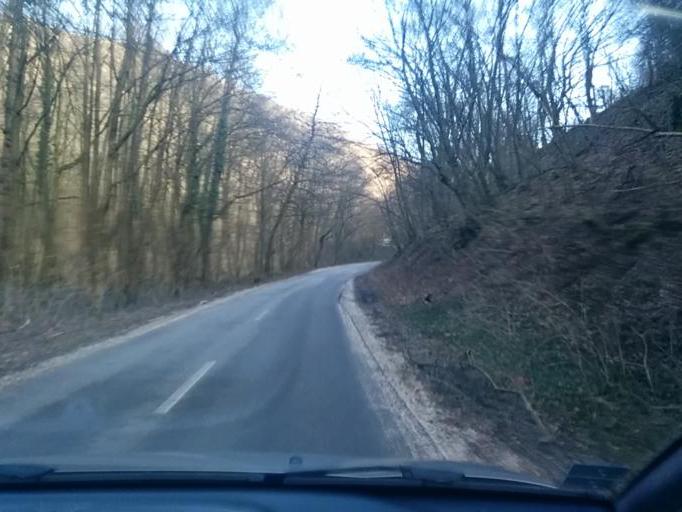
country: SK
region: Nitriansky
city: Cachtice
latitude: 48.7382
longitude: 17.7683
